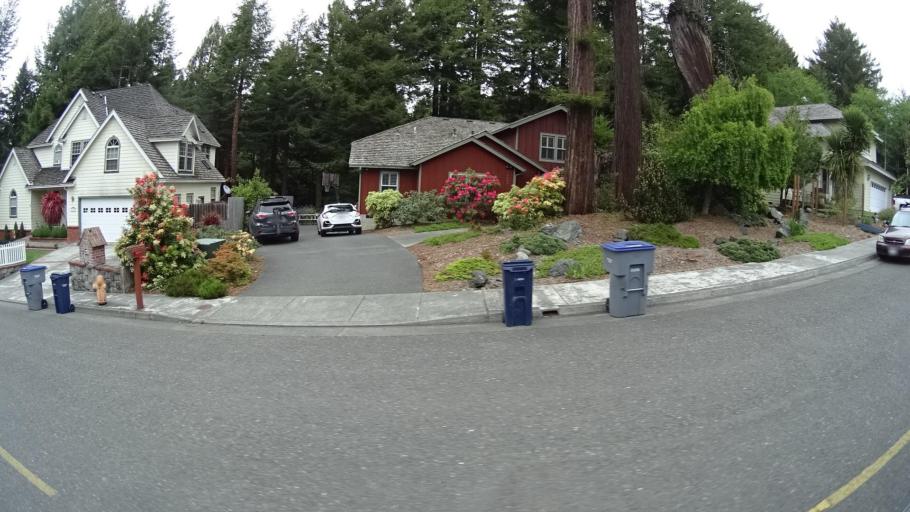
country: US
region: California
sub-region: Humboldt County
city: Arcata
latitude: 40.8840
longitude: -124.0699
